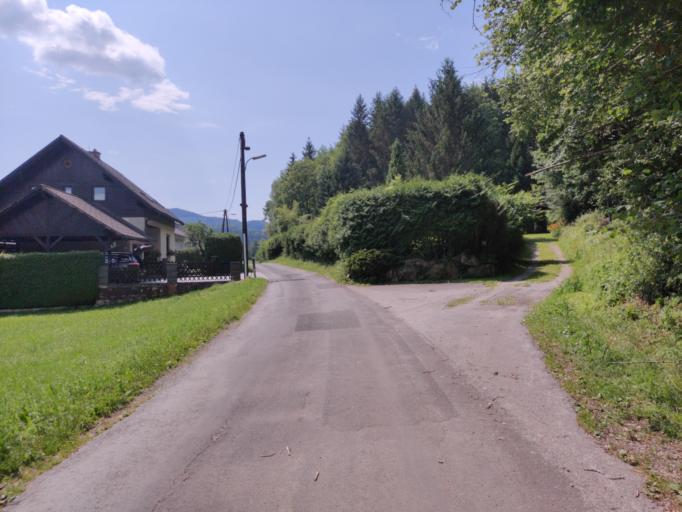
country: AT
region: Styria
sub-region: Politischer Bezirk Graz-Umgebung
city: Gratwein
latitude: 47.1185
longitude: 15.2967
